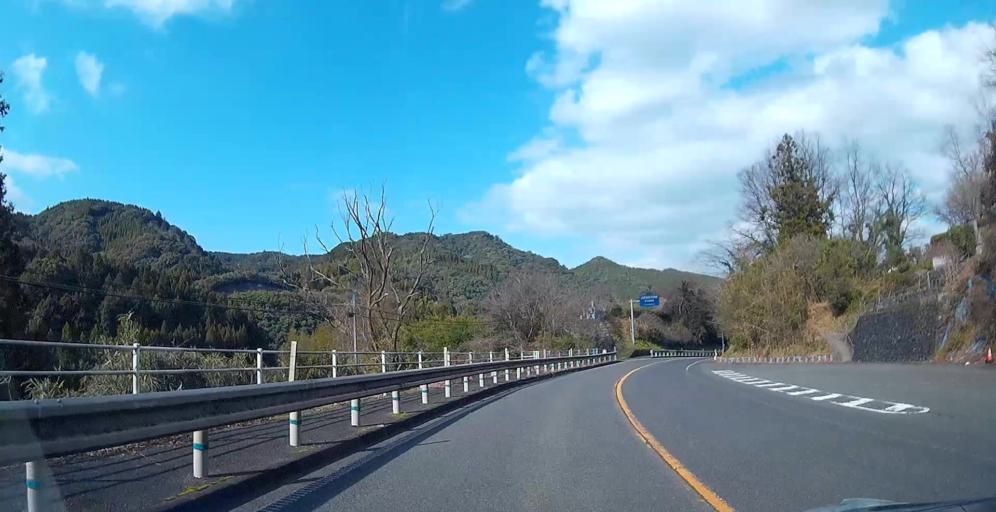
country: JP
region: Kumamoto
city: Yatsushiro
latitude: 32.3918
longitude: 130.5444
